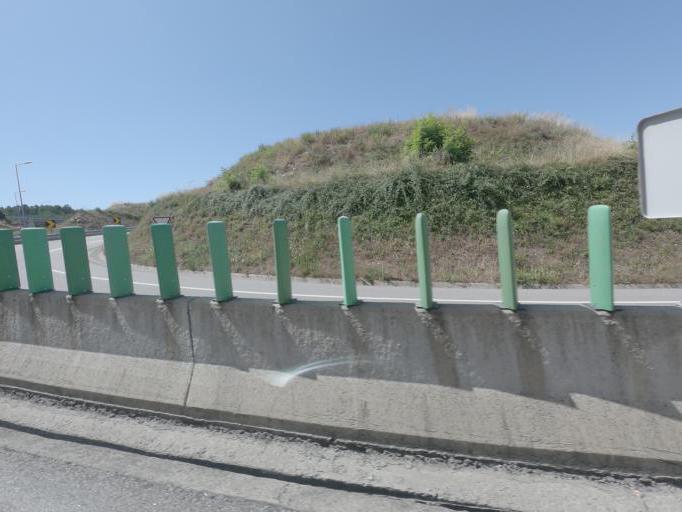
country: PT
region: Vila Real
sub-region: Vila Real
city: Vila Real
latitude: 41.2804
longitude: -7.7189
